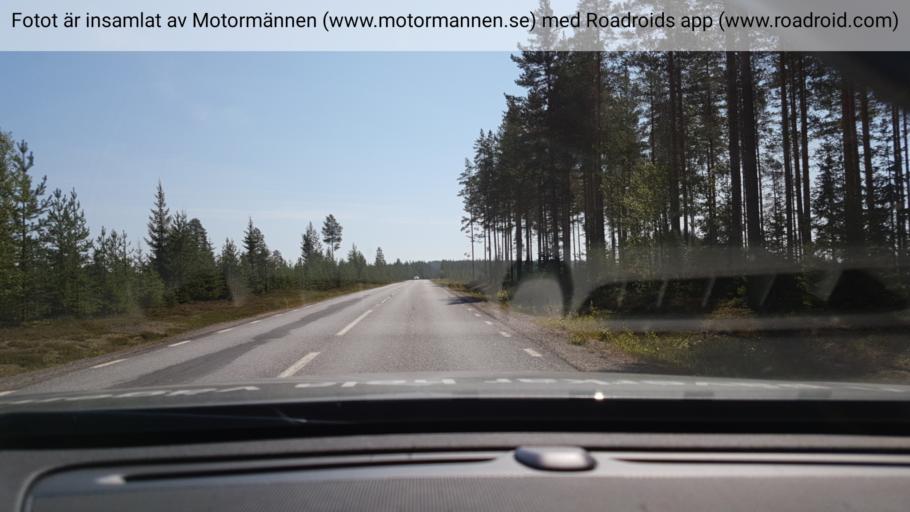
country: SE
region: Vaesterbotten
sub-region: Vindelns Kommun
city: Vindeln
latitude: 64.2382
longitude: 19.6952
